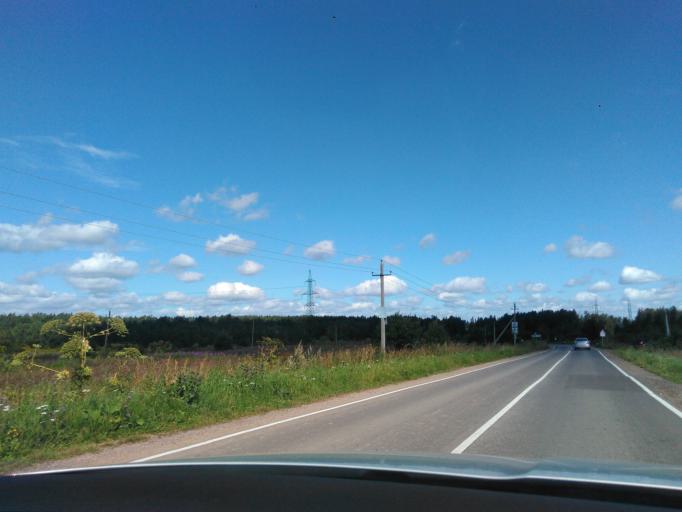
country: RU
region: Moskovskaya
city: Klin
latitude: 56.1994
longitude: 36.8139
